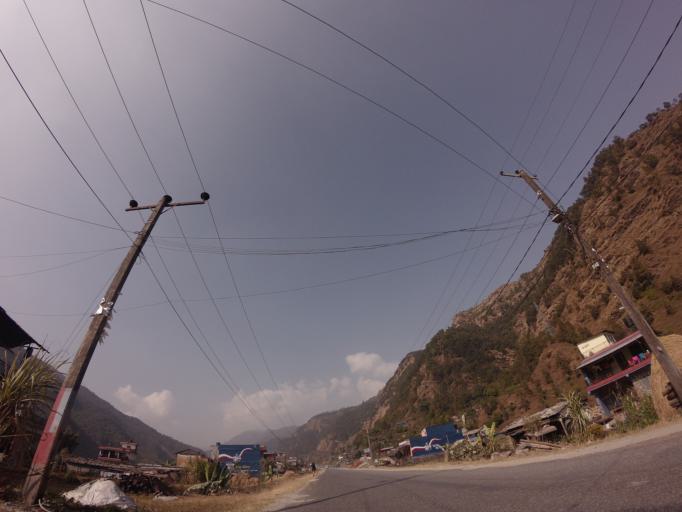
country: NP
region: Western Region
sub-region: Gandaki Zone
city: Pokhara
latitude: 28.2866
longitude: 83.9002
